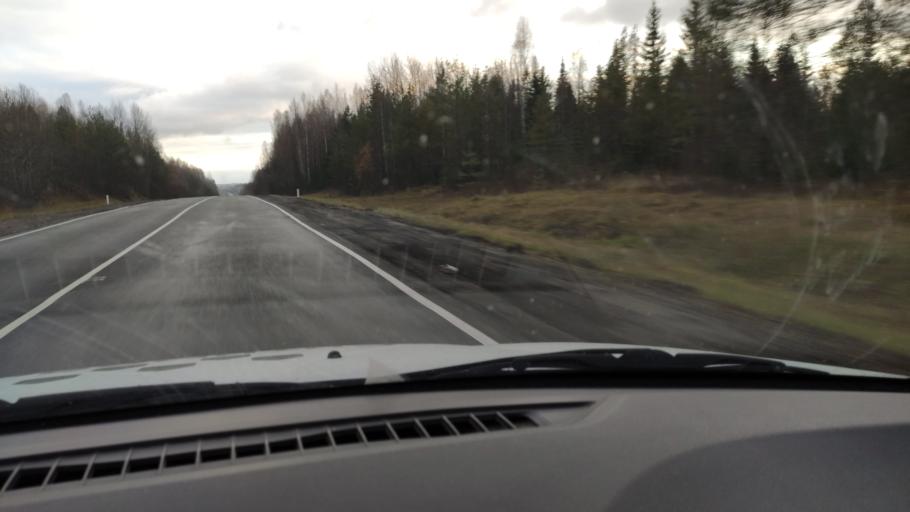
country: RU
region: Kirov
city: Omutninsk
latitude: 58.7428
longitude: 52.0655
